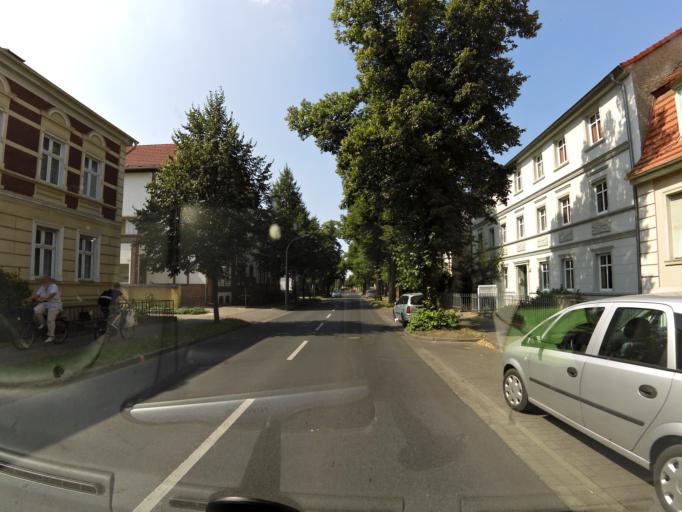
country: DE
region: Brandenburg
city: Zehdenick
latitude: 52.9781
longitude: 13.3266
